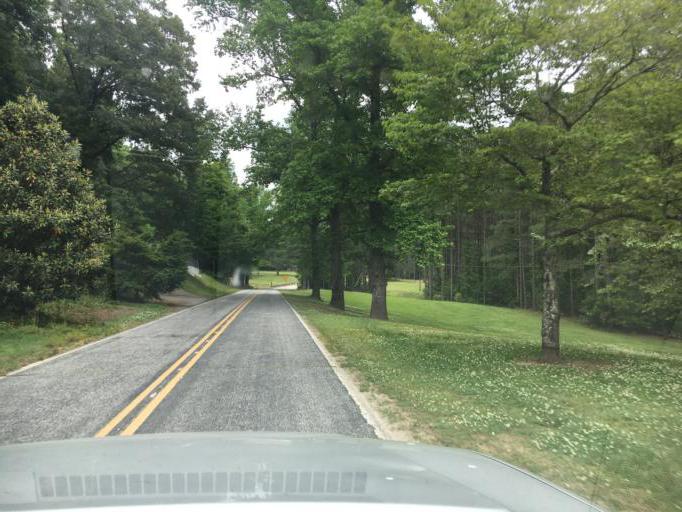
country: US
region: South Carolina
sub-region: Greenville County
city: Tigerville
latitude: 35.1344
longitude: -82.4190
